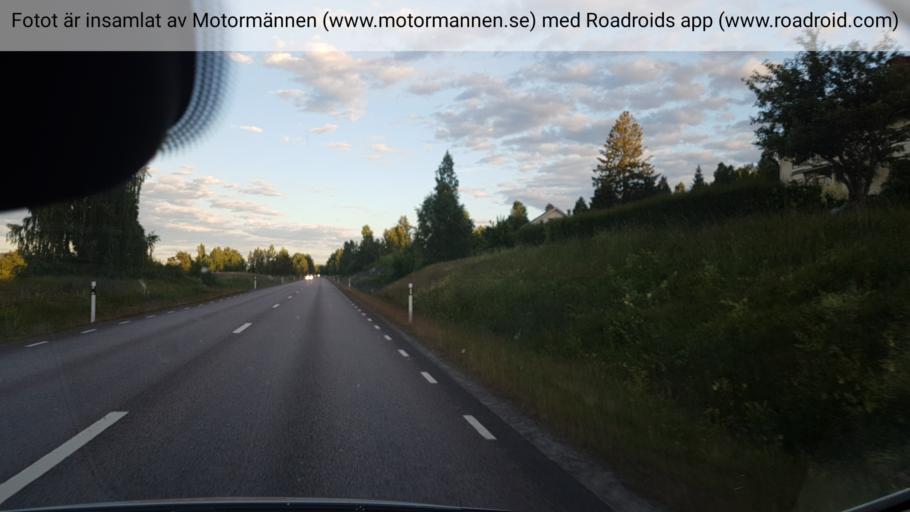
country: SE
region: Vaermland
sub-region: Sunne Kommun
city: Sunne
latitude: 59.9349
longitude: 13.1236
